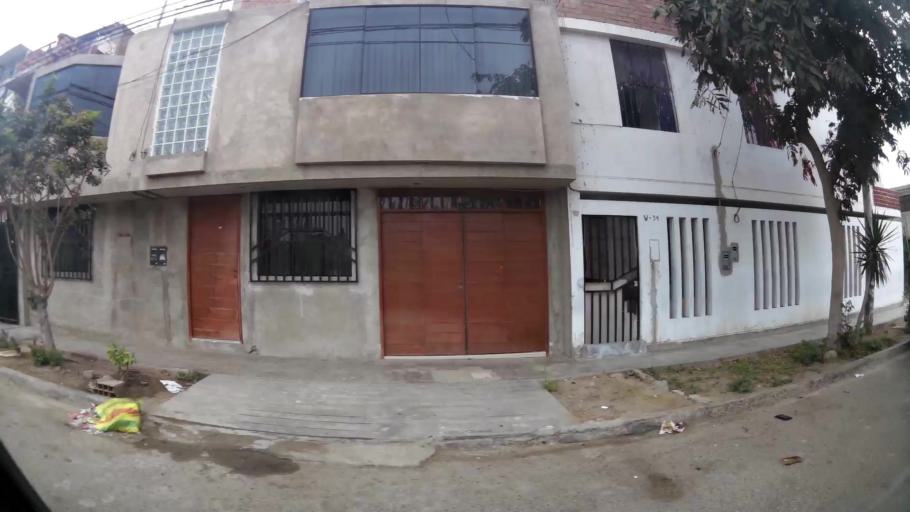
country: PE
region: La Libertad
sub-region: Provincia de Trujillo
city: Trujillo
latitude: -8.1108
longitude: -79.0434
